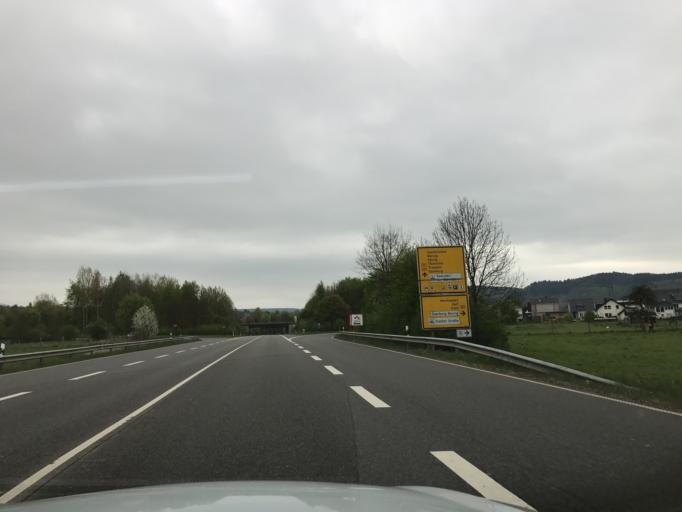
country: DE
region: Rheinland-Pfalz
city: Ockfen
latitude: 49.6096
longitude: 6.5671
